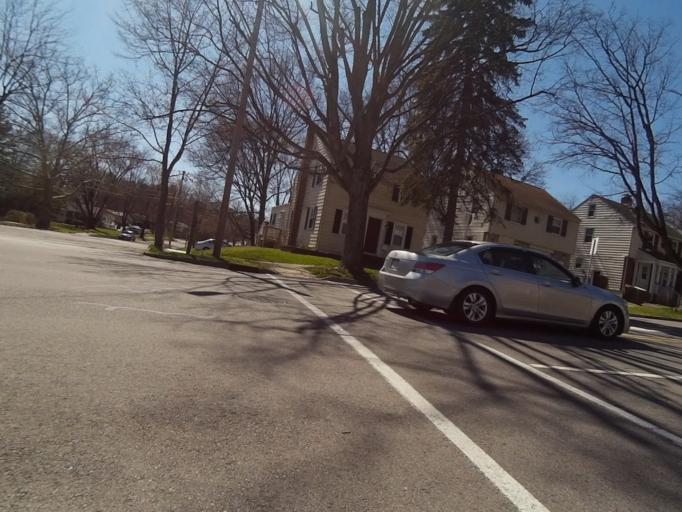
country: US
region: Pennsylvania
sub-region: Centre County
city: State College
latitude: 40.7896
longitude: -77.8530
